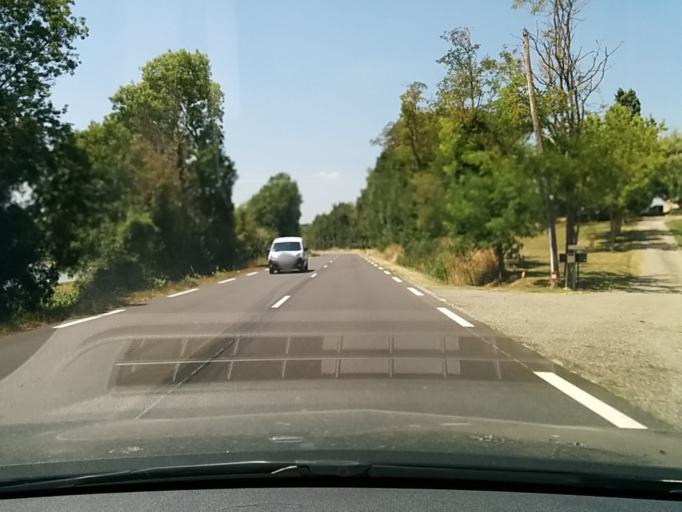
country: FR
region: Midi-Pyrenees
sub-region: Departement du Gers
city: Gimont
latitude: 43.6167
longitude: 0.9300
